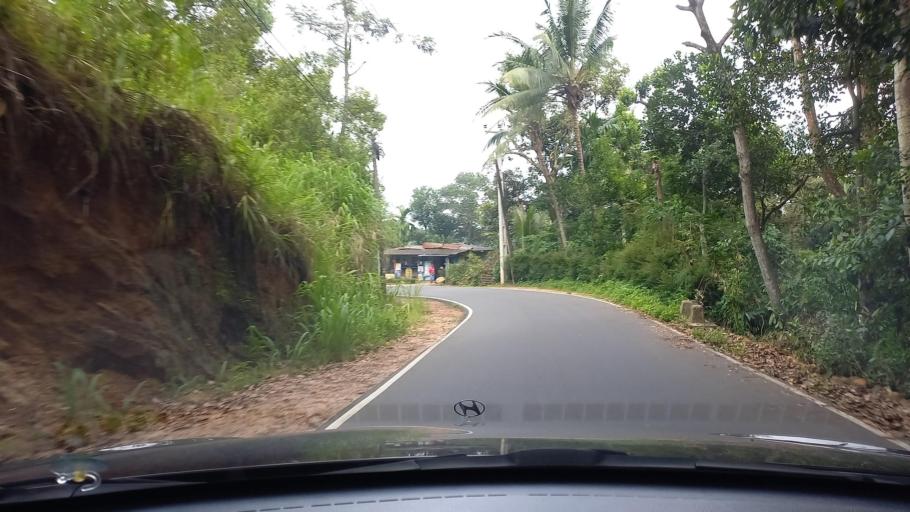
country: LK
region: Central
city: Gampola
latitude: 7.2248
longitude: 80.6068
